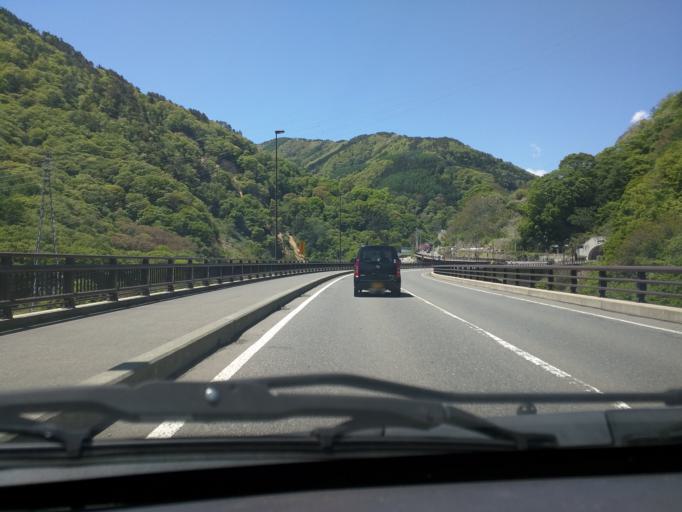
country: JP
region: Nagano
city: Nagano-shi
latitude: 36.6611
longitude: 138.1693
